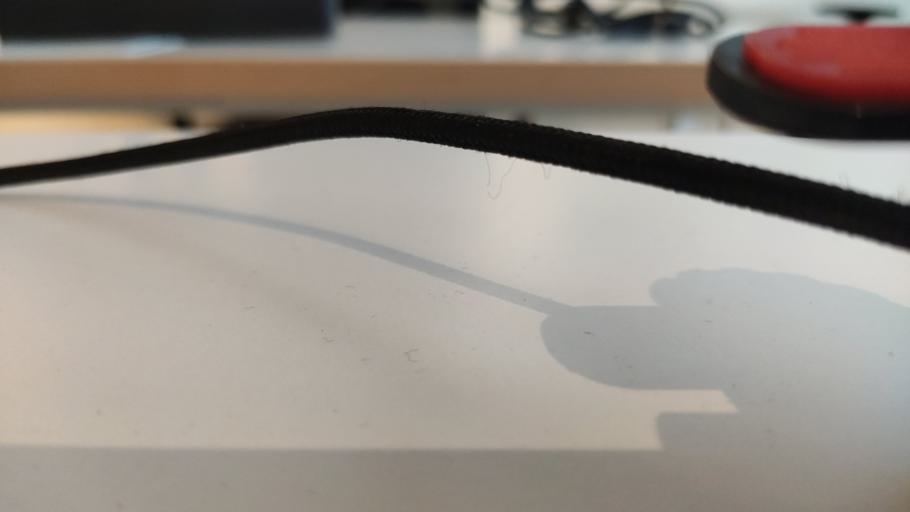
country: RU
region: Moskovskaya
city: Novopetrovskoye
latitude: 55.9797
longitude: 36.4504
